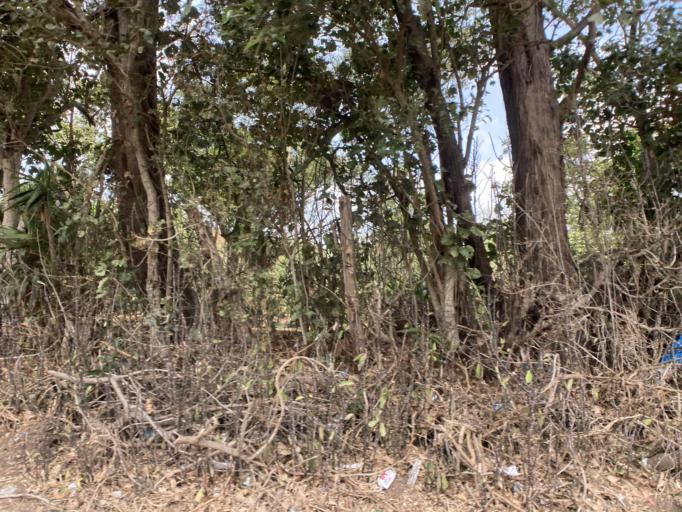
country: GT
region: Escuintla
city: San Vicente Pacaya
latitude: 14.3440
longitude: -90.5705
